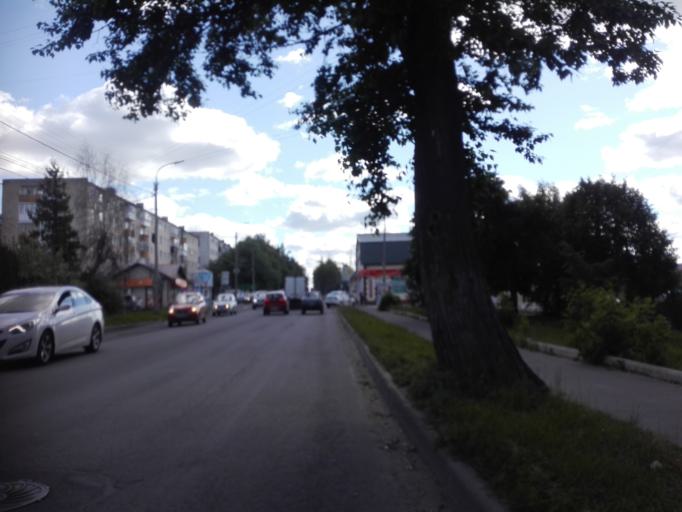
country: RU
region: Orjol
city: Orel
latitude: 52.9521
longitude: 36.0436
